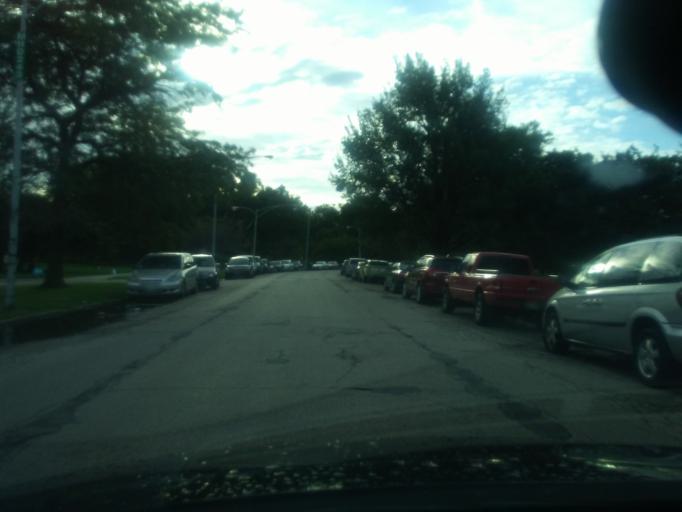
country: US
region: Illinois
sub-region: Cook County
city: Evanston
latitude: 41.9633
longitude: -87.6366
